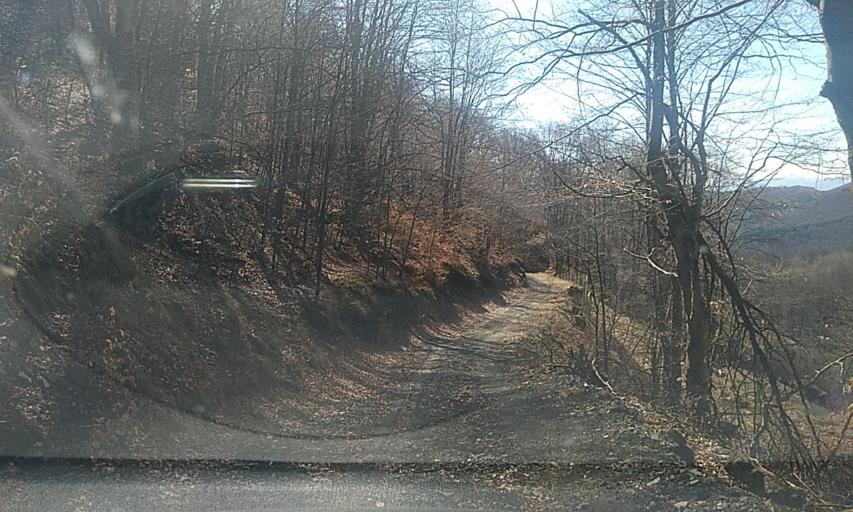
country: RS
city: Radovnica
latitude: 42.3518
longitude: 22.3380
